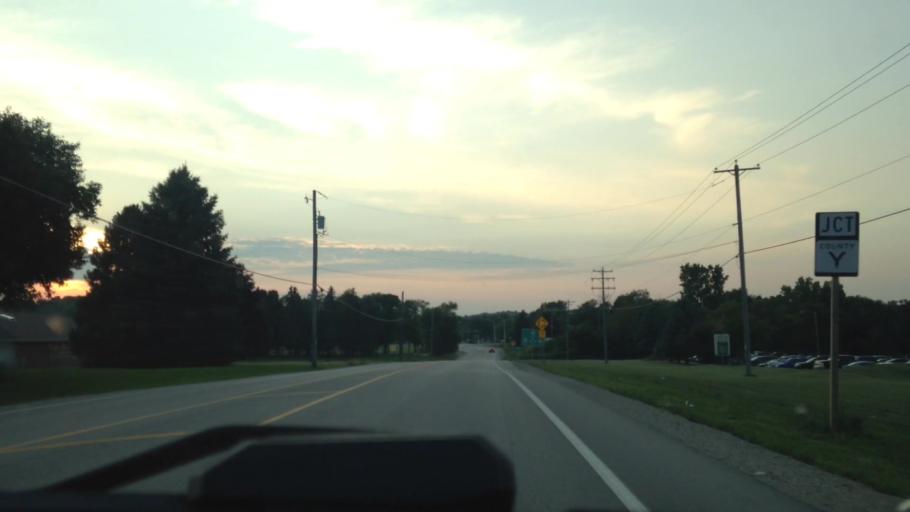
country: US
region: Wisconsin
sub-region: Waukesha County
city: Menomonee Falls
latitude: 43.2036
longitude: -88.1534
